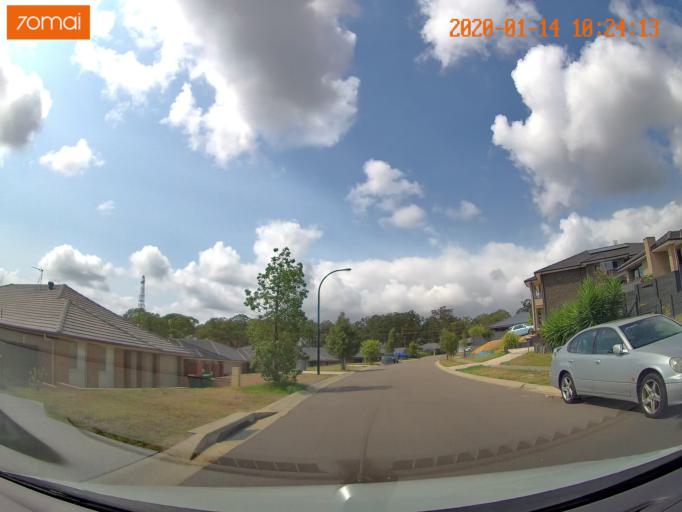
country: AU
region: New South Wales
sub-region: Lake Macquarie Shire
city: Dora Creek
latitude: -33.1104
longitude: 151.5105
